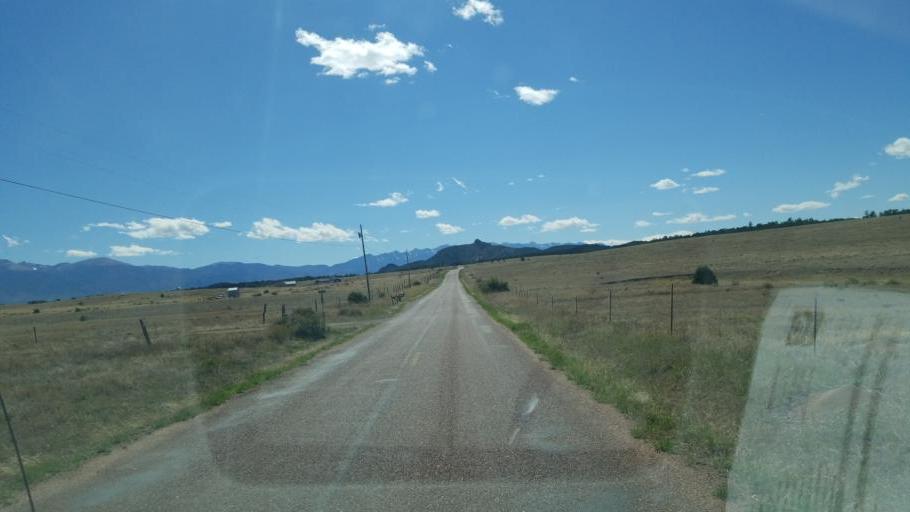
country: US
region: Colorado
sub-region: Custer County
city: Westcliffe
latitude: 38.3497
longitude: -105.4877
